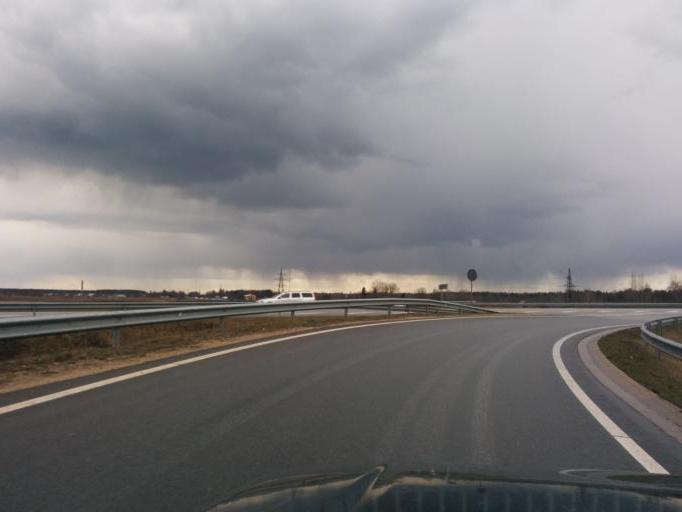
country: LV
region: Marupe
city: Marupe
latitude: 56.8337
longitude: 24.0415
